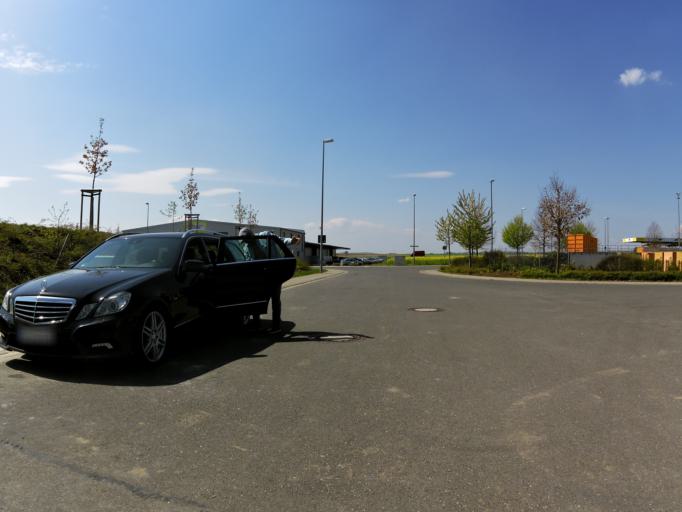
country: DE
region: Bavaria
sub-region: Regierungsbezirk Unterfranken
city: Giebelstadt
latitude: 49.6893
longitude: 9.9457
